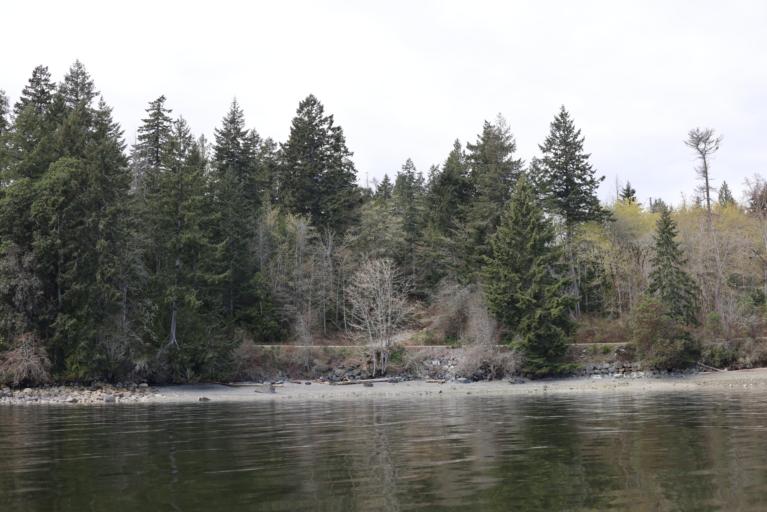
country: CA
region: British Columbia
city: North Saanich
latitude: 48.6306
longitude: -123.5282
